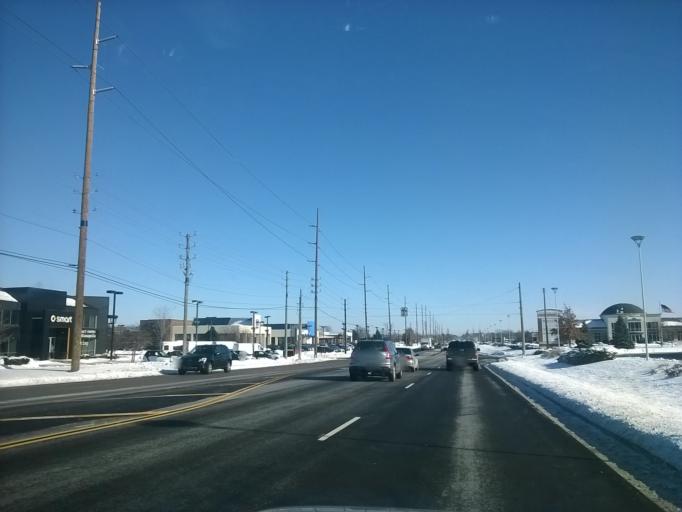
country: US
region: Indiana
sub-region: Hamilton County
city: Carmel
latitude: 39.9269
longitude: -86.1047
